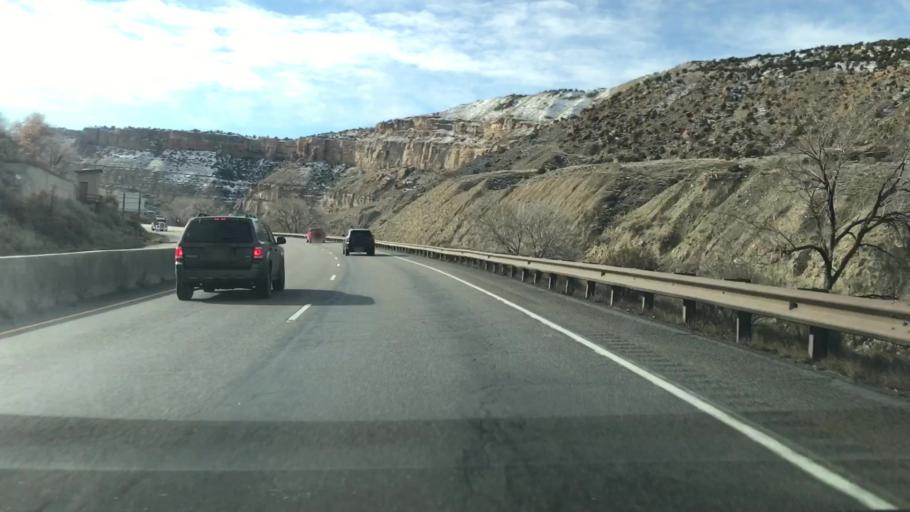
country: US
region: Colorado
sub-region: Mesa County
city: Palisade
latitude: 39.1363
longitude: -108.3212
